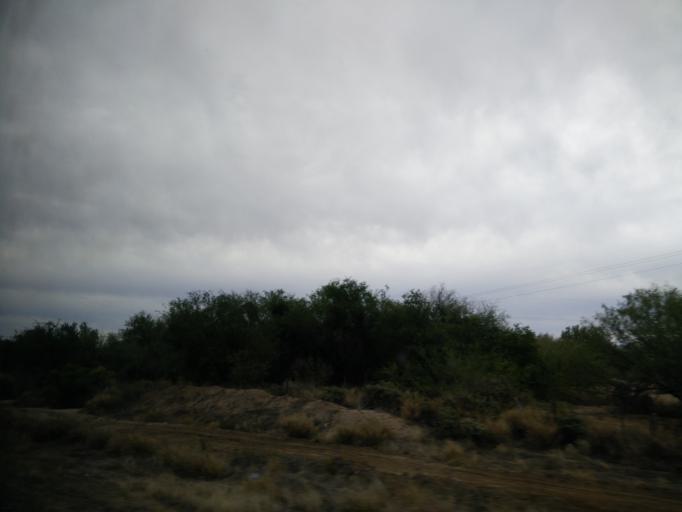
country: MX
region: Sonora
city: Hermosillo
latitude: 28.6847
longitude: -110.9913
